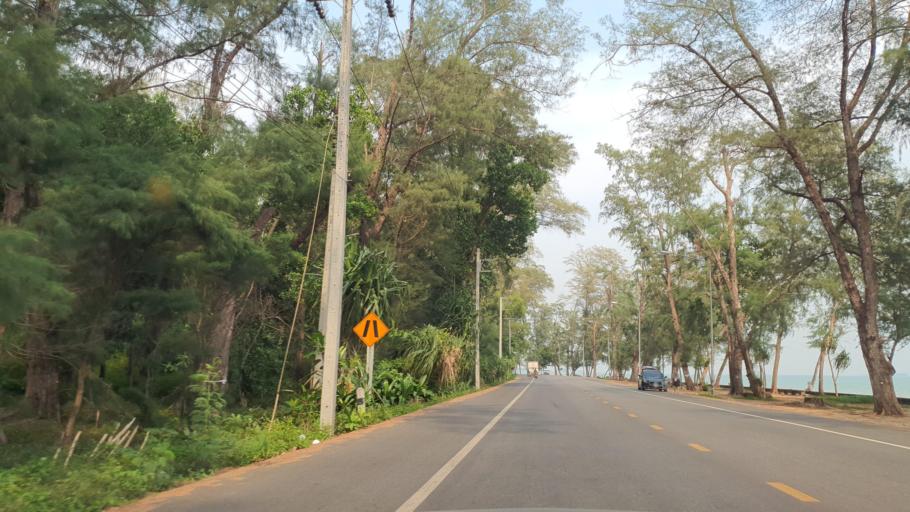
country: TH
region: Rayong
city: Rayong
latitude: 12.6319
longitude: 101.4543
